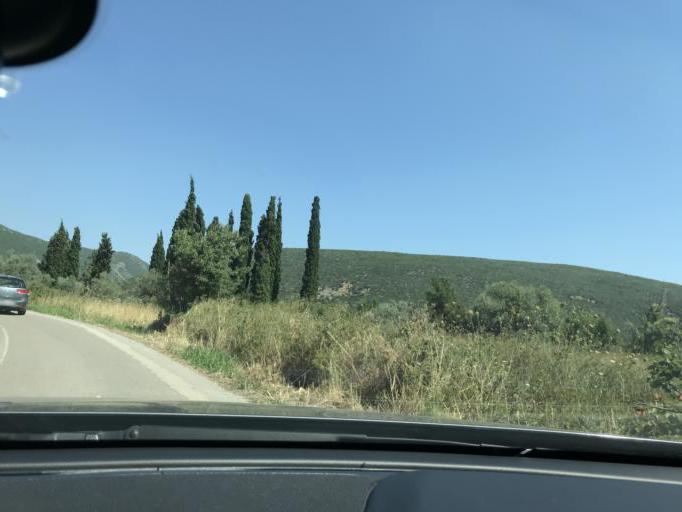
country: GR
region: Central Greece
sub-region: Nomos Fthiotidos
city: Kato Tithorea
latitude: 38.5193
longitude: 22.7468
